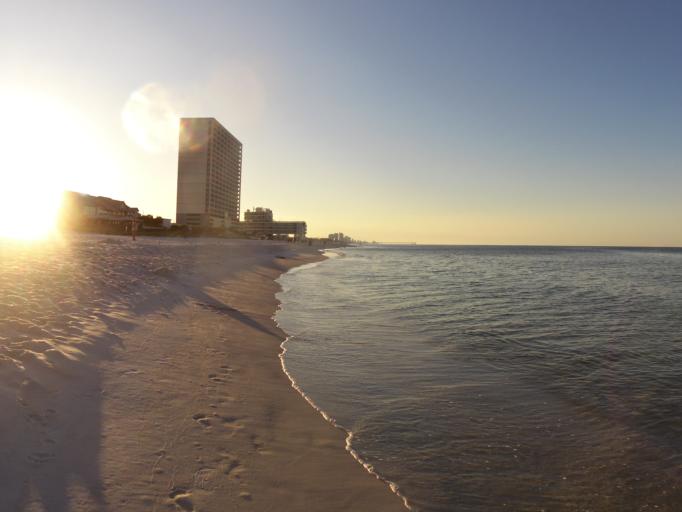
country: US
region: Florida
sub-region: Bay County
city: Panama City Beach
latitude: 30.2048
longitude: -85.8588
